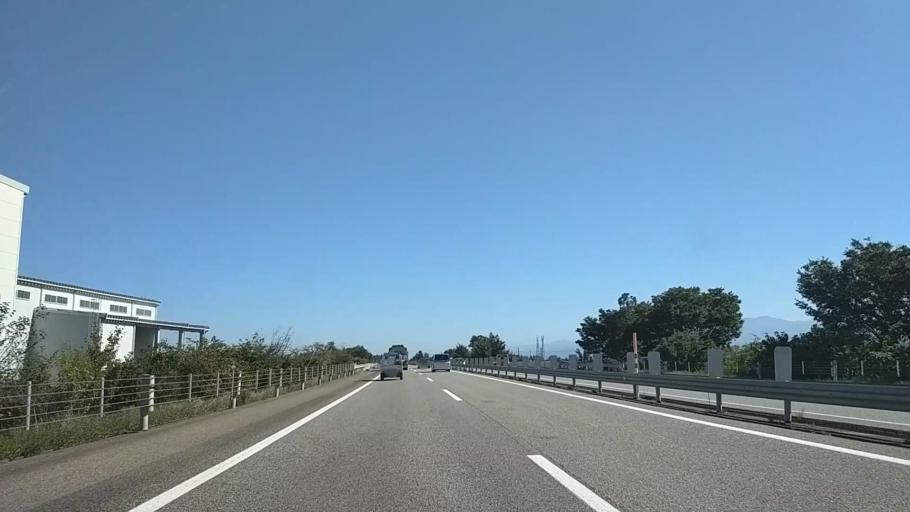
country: JP
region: Toyama
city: Toyama-shi
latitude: 36.6541
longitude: 137.2548
